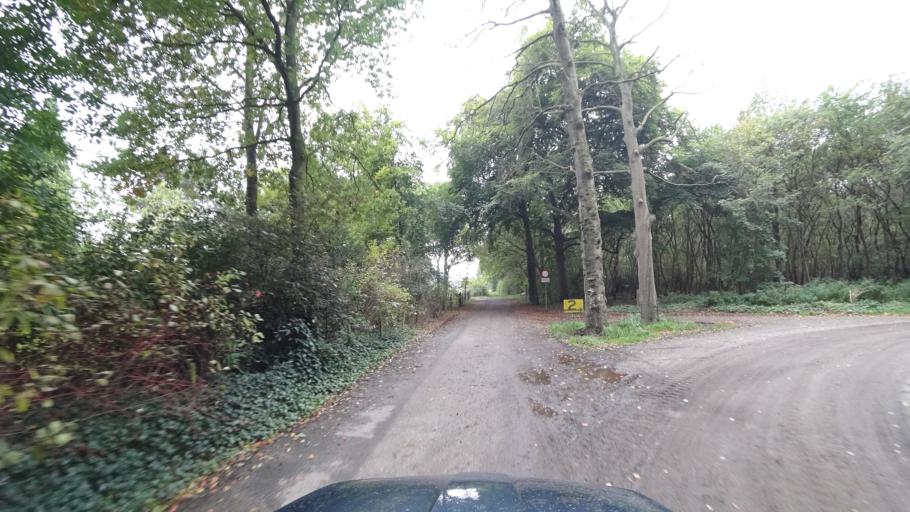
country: NL
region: Utrecht
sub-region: Gemeente Zeist
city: Zeist
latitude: 52.0690
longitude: 5.2505
